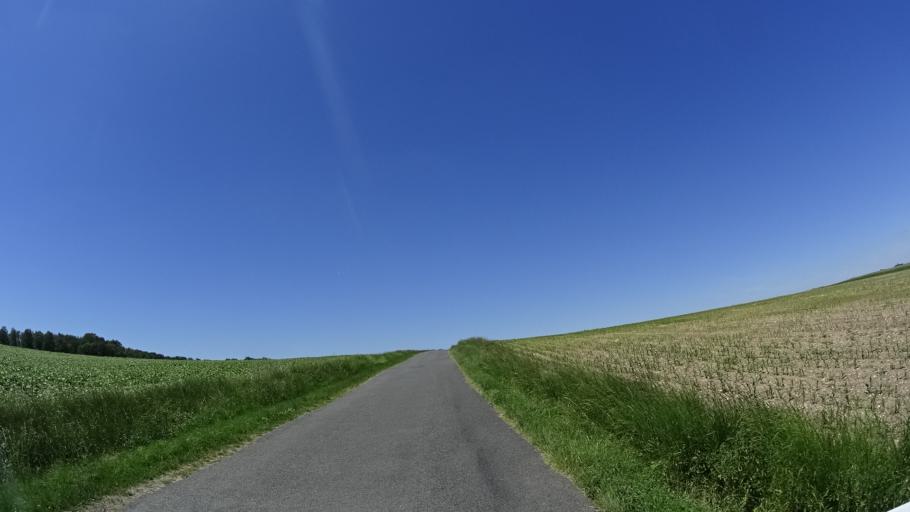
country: FR
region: Pays de la Loire
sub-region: Departement de Maine-et-Loire
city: Chenehutte-Treves-Cunault
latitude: 47.2848
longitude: -0.1399
